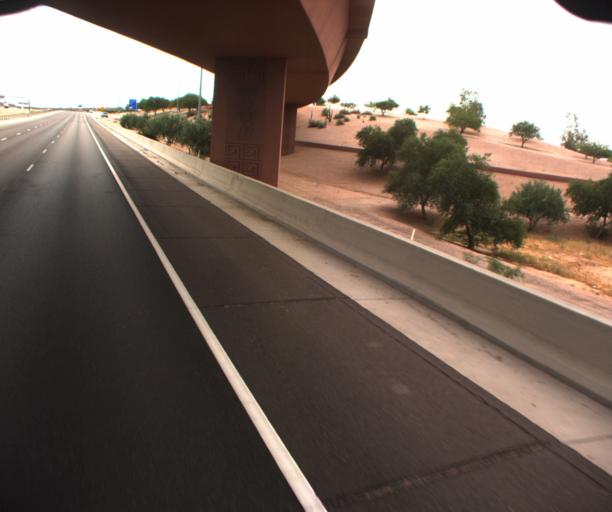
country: US
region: Arizona
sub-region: Pinal County
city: Apache Junction
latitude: 33.3853
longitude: -111.6484
